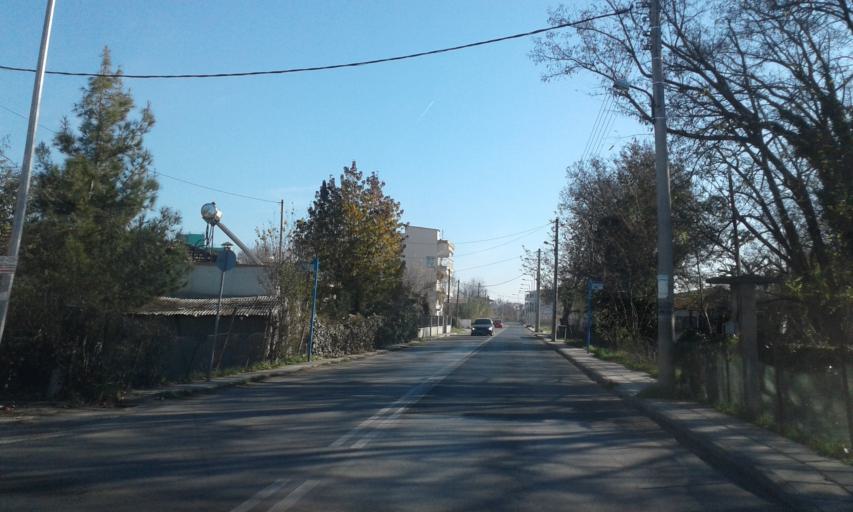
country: GR
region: Central Macedonia
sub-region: Nomos Thessalonikis
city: Lagkadas
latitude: 40.7461
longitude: 23.0659
